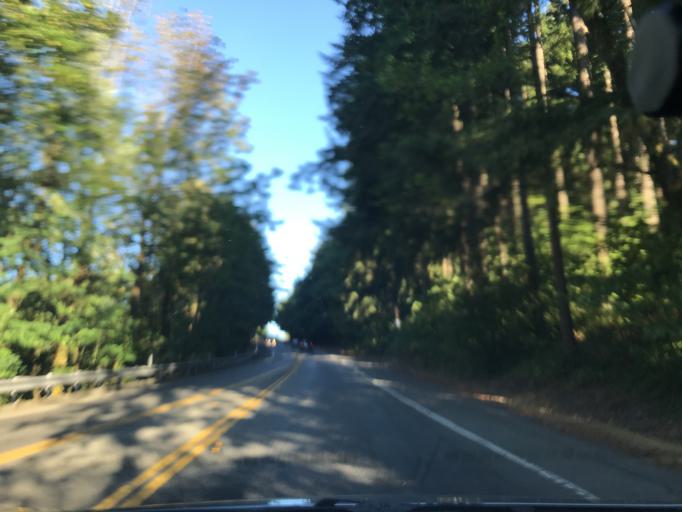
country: US
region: Washington
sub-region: King County
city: Pacific
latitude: 47.2609
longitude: -122.1920
